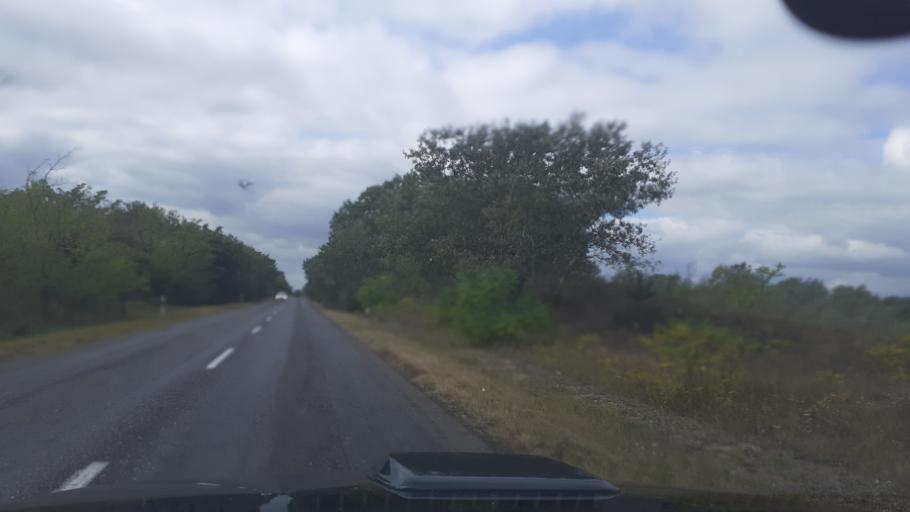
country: HU
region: Bacs-Kiskun
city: Agasegyhaza
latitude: 46.8677
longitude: 19.4142
